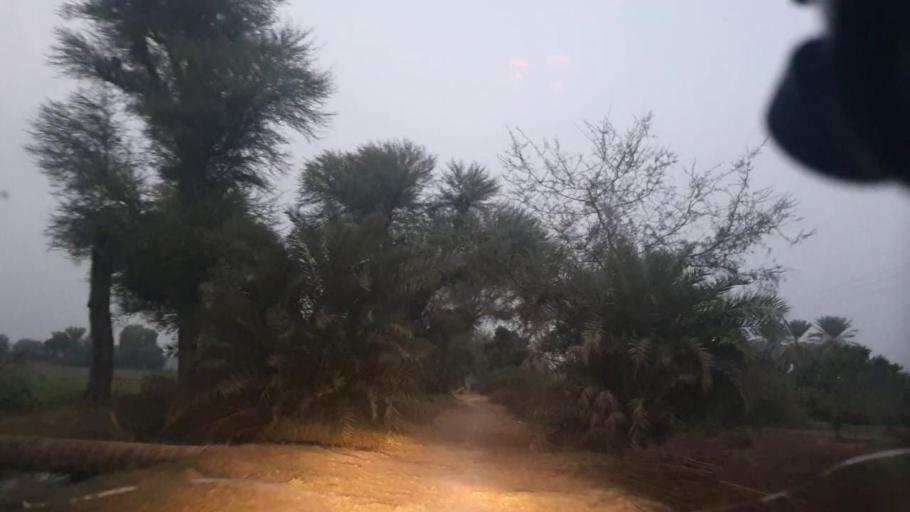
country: PK
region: Sindh
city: Hingorja
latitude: 27.1971
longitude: 68.3717
